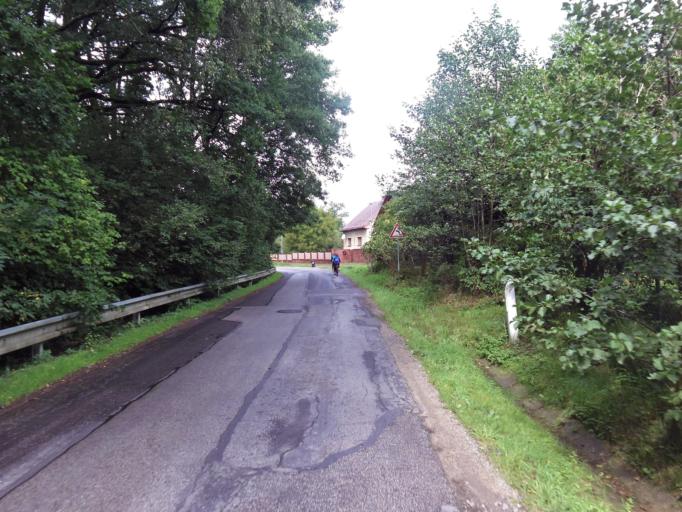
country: CZ
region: Jihocesky
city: Suchdol nad Luznici
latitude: 48.9065
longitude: 14.9094
